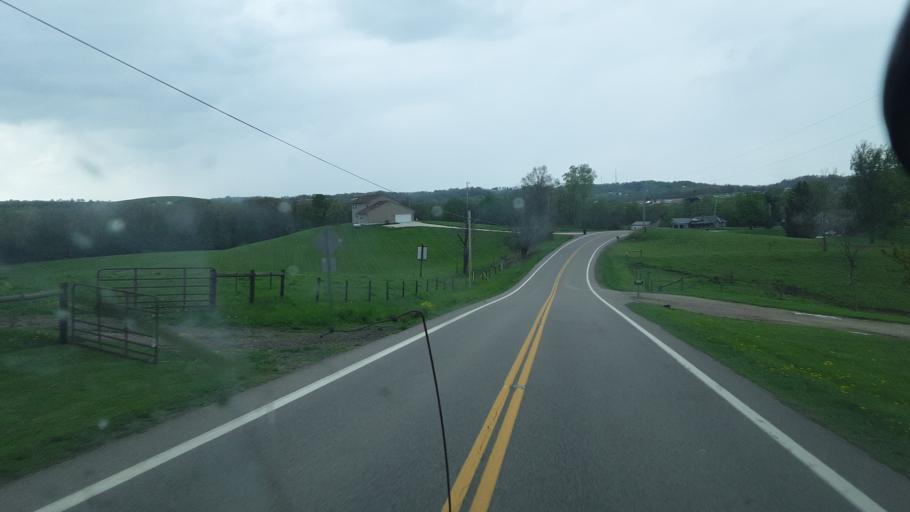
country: US
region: Ohio
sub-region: Muskingum County
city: New Concord
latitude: 39.9533
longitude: -81.7104
